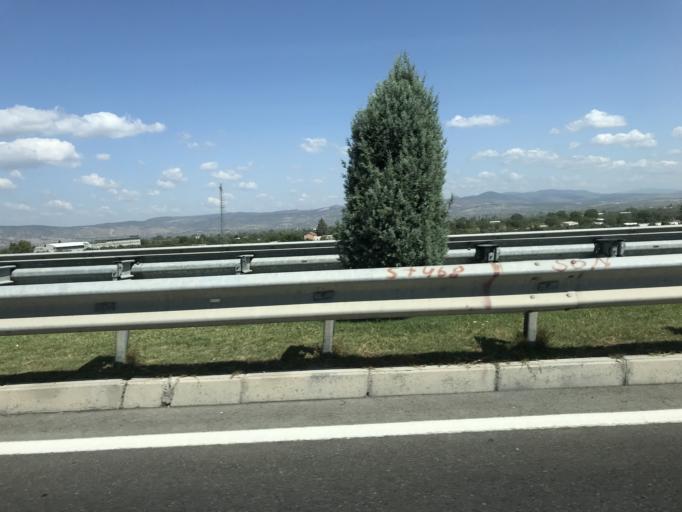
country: TR
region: Manisa
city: Muradiye
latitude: 38.6400
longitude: 27.3748
